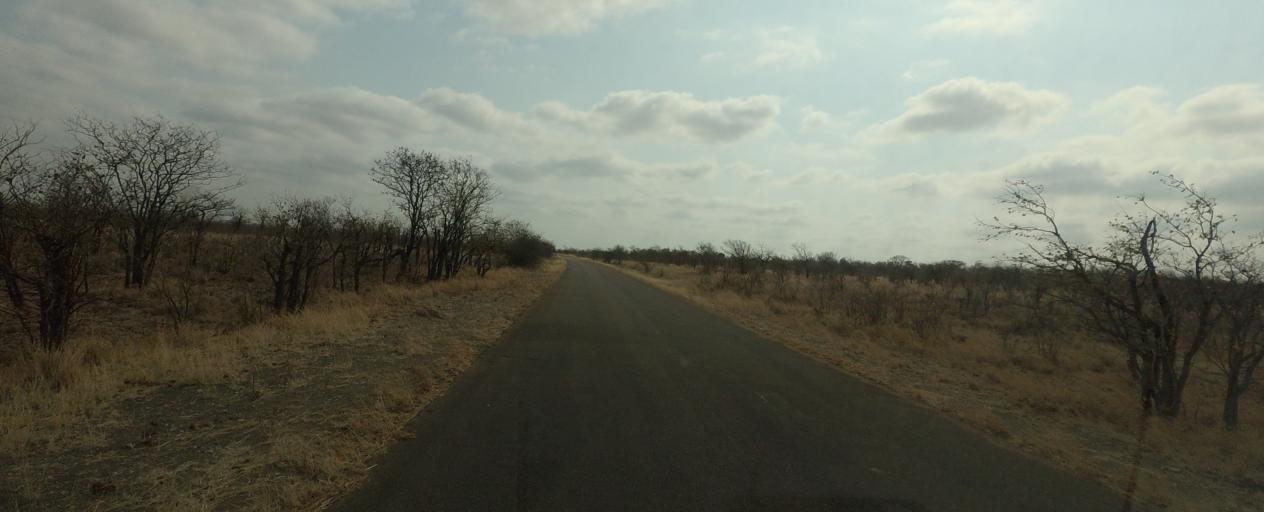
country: ZA
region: Limpopo
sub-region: Vhembe District Municipality
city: Mutale
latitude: -22.5728
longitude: 31.1898
